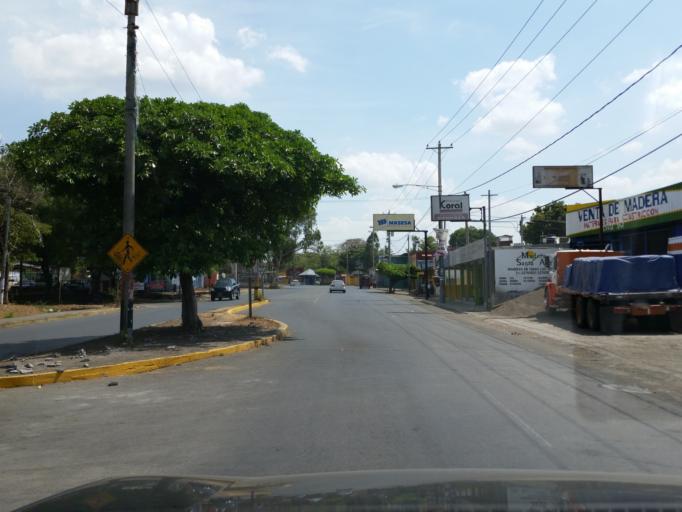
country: NI
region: Managua
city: Managua
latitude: 12.1277
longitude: -86.2445
